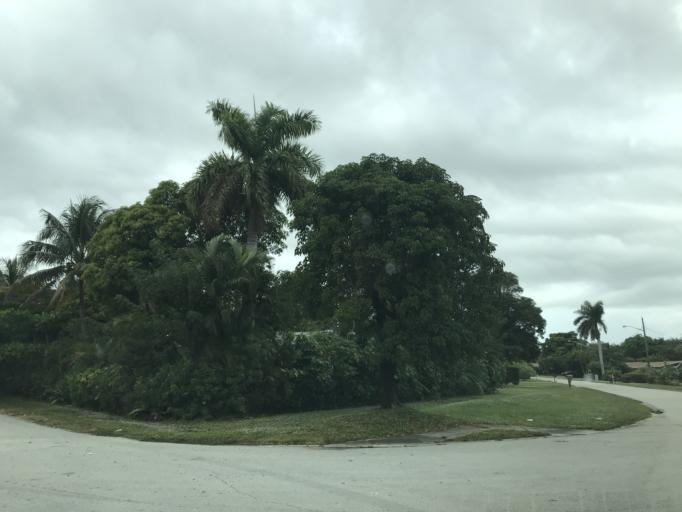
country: US
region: Florida
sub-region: Palm Beach County
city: Delray Beach
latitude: 26.4698
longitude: -80.0950
